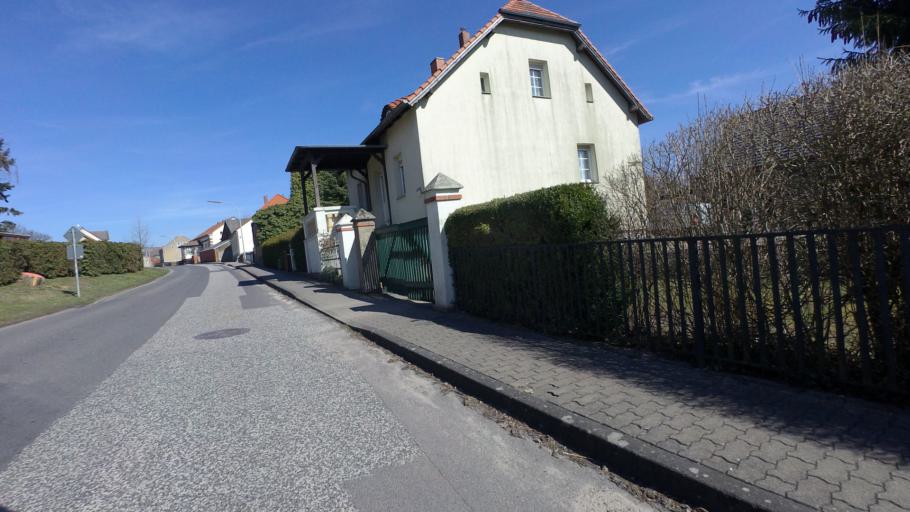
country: DE
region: Brandenburg
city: Furstenwalde
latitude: 52.4296
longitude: 14.0428
